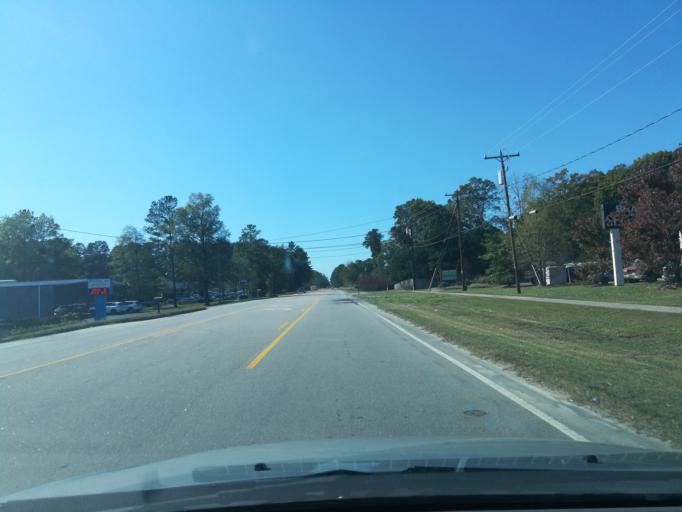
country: US
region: North Carolina
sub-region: Durham County
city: Durham
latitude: 36.0333
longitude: -78.9759
